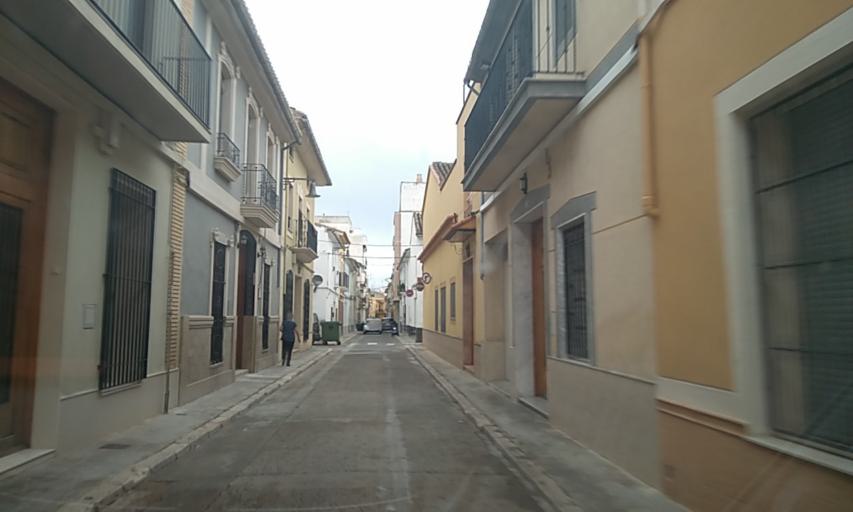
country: ES
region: Valencia
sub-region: Provincia de Valencia
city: L'Alcudia
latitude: 39.1968
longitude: -0.5061
